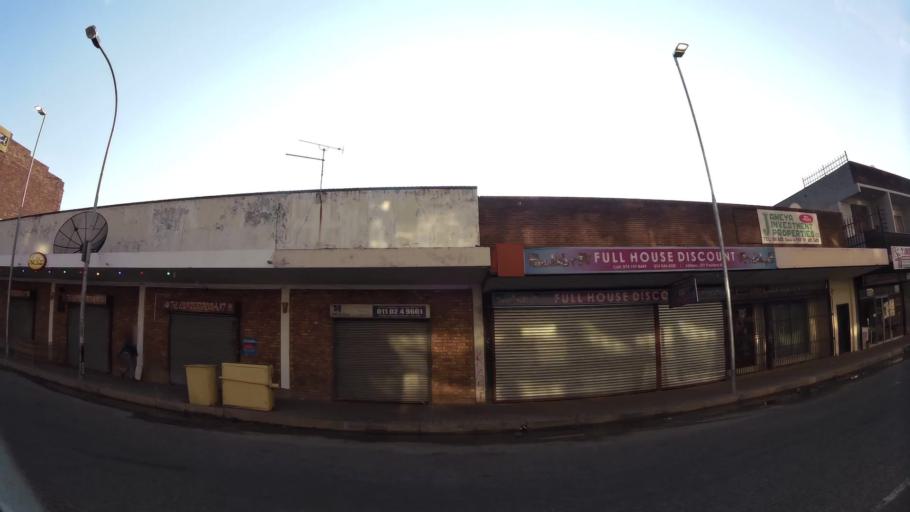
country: ZA
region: Gauteng
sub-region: Ekurhuleni Metropolitan Municipality
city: Germiston
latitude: -26.2178
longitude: 28.1662
